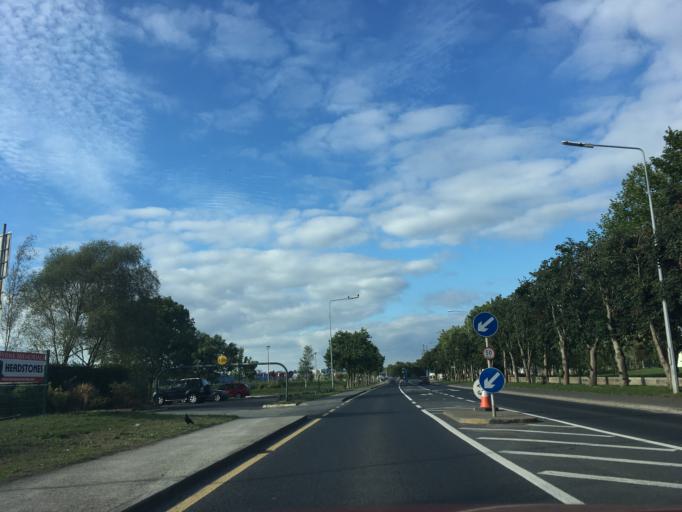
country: IE
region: Leinster
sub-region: Loch Garman
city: New Ross
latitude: 52.3899
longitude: -6.9511
